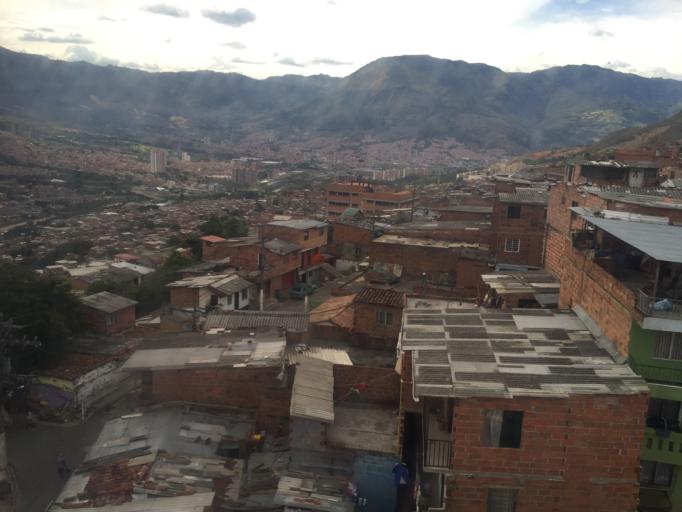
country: CO
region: Antioquia
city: Bello
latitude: 6.2954
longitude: -75.5489
